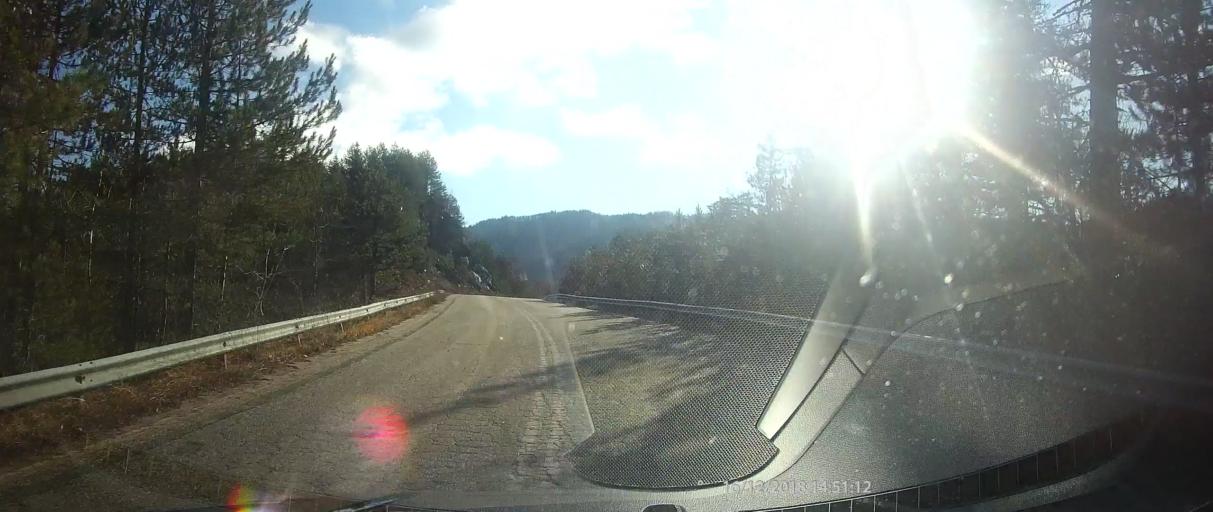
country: GR
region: West Macedonia
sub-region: Nomos Kastorias
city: Nestorio
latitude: 40.2062
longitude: 21.0738
